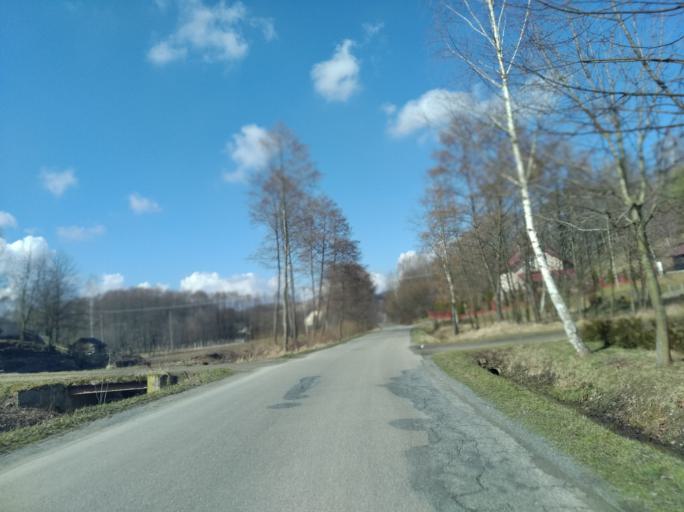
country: PL
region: Subcarpathian Voivodeship
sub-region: Powiat debicki
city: Brzostek
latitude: 49.8933
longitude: 21.4911
